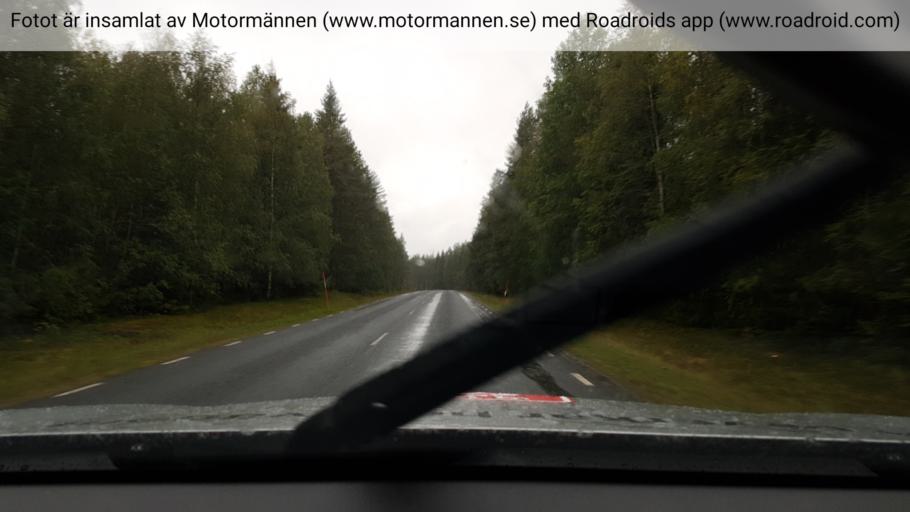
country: SE
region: Vaesterbotten
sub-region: Skelleftea Kommun
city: Storvik
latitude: 64.9626
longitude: 20.6486
